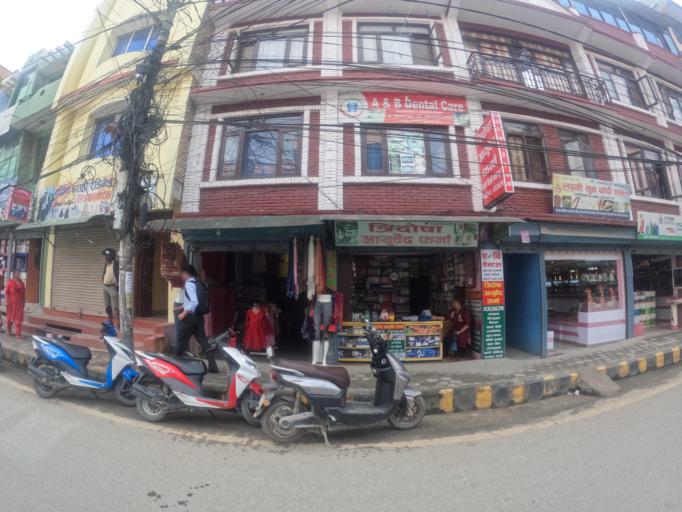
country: NP
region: Central Region
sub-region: Bagmati Zone
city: Bhaktapur
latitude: 27.6698
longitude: 85.3859
